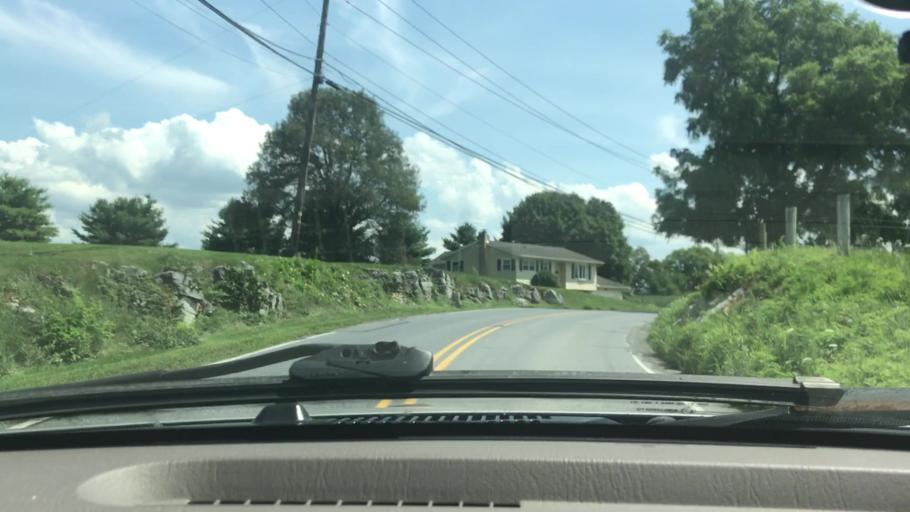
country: US
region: Pennsylvania
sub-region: Dauphin County
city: Hummelstown
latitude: 40.2467
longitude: -76.7357
